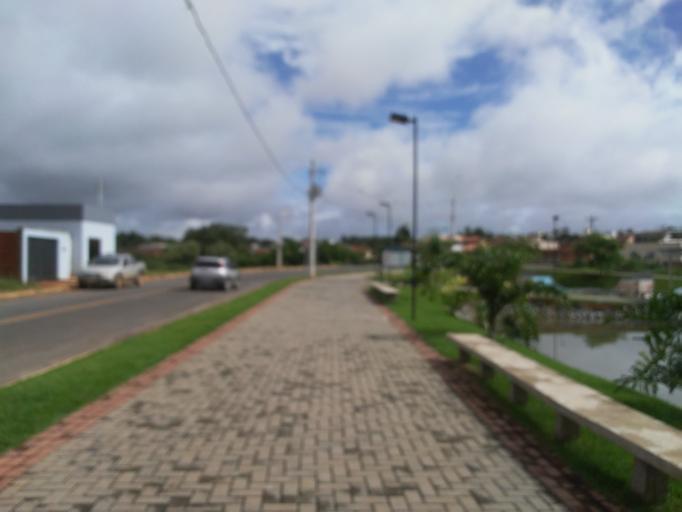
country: BR
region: Goias
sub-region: Ipameri
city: Ipameri
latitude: -17.7191
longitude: -48.1672
